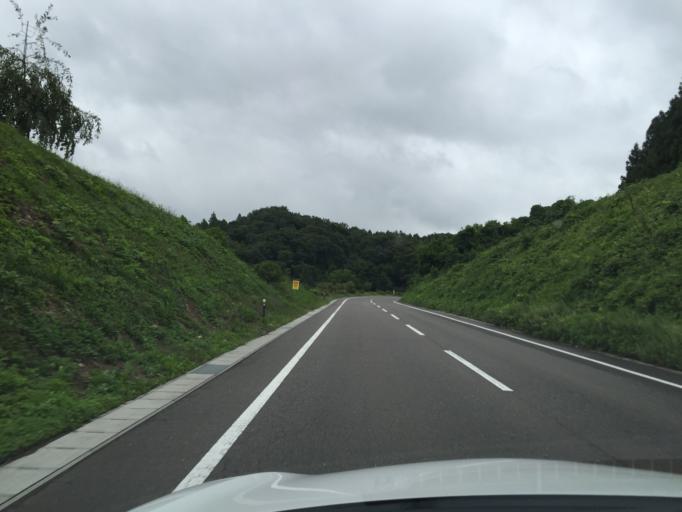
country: JP
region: Fukushima
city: Miharu
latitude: 37.4506
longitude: 140.5271
